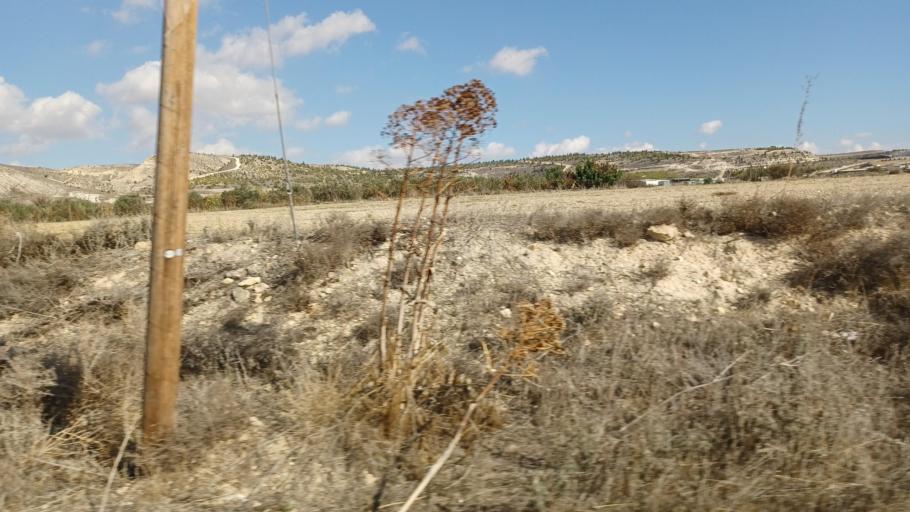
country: CY
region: Larnaka
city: Voroklini
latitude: 35.0066
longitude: 33.6483
